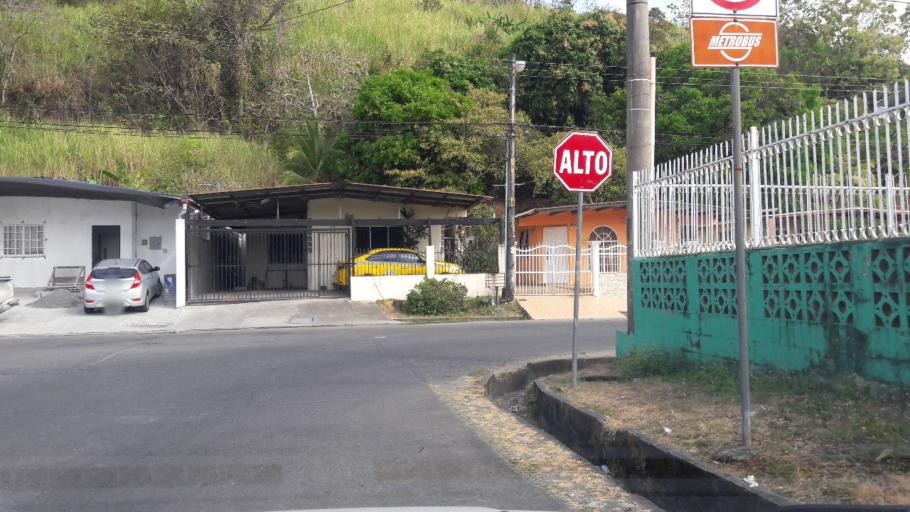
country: PA
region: Panama
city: San Miguelito
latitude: 9.0464
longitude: -79.5139
